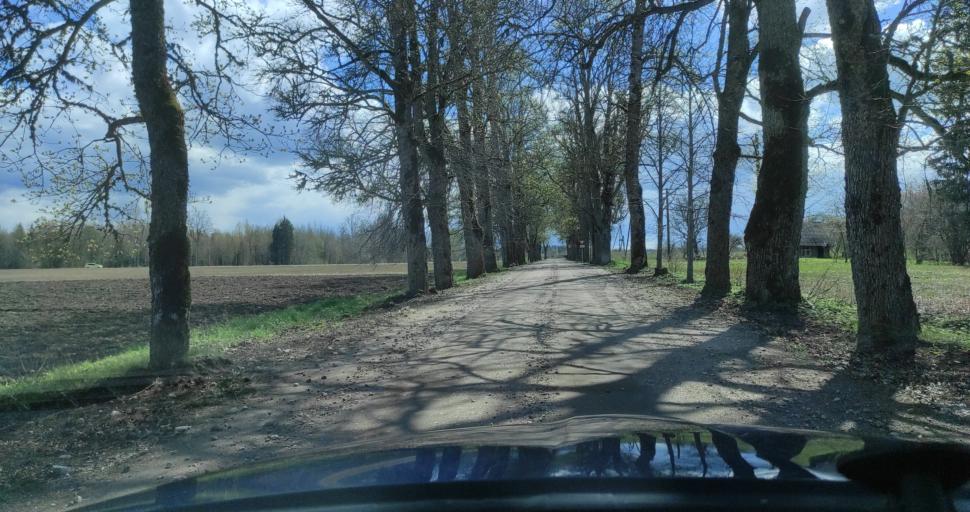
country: LV
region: Kuldigas Rajons
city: Kuldiga
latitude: 56.8591
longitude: 21.8134
